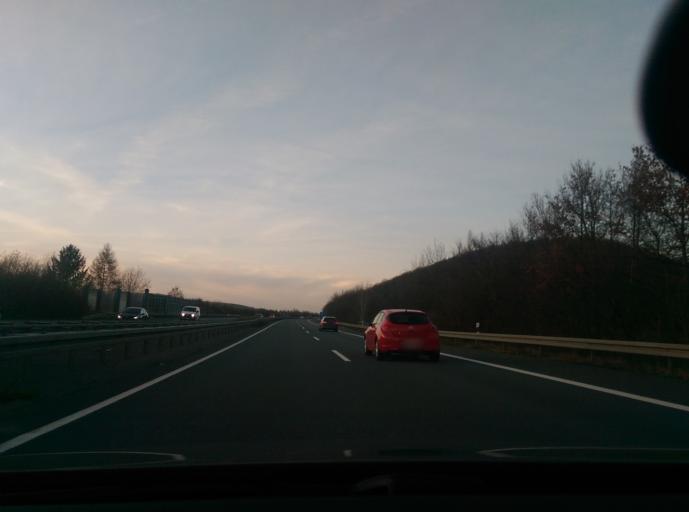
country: DE
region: Lower Saxony
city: Gemeinde Friedland
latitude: 51.4234
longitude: 9.8971
